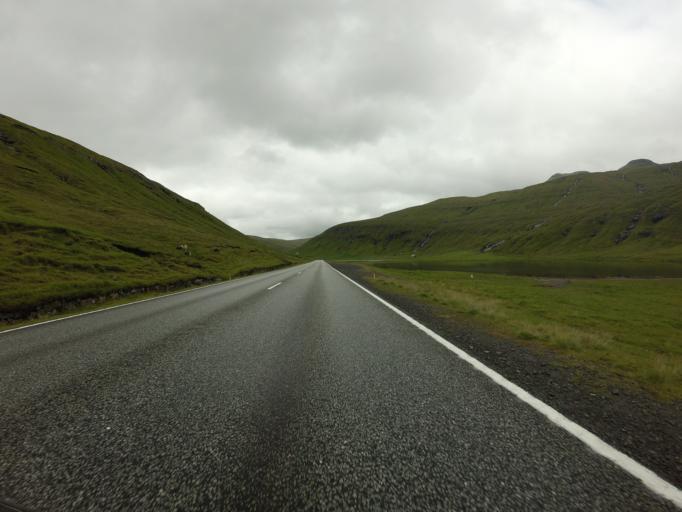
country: FO
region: Streymoy
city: Kollafjordhur
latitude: 62.1235
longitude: -6.9938
